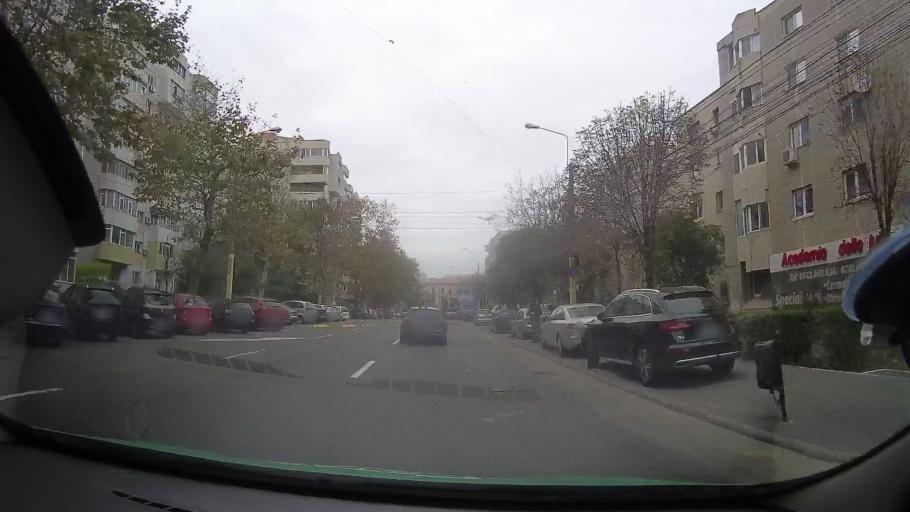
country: RO
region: Constanta
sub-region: Municipiul Constanta
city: Constanta
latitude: 44.1797
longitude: 28.6529
